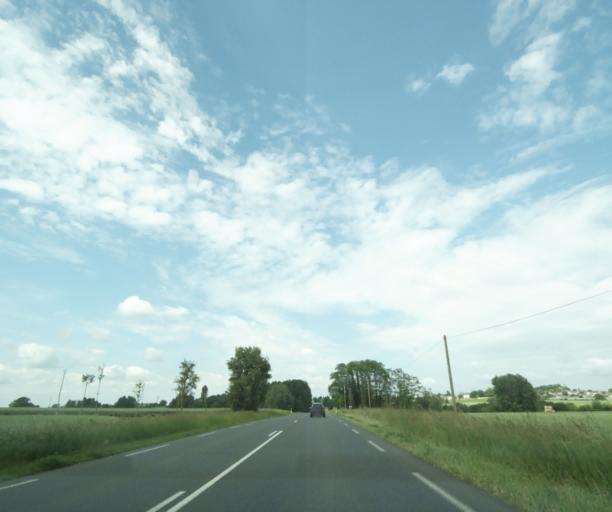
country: FR
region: Pays de la Loire
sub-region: Departement de Maine-et-Loire
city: Distre
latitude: 47.1879
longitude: -0.1295
